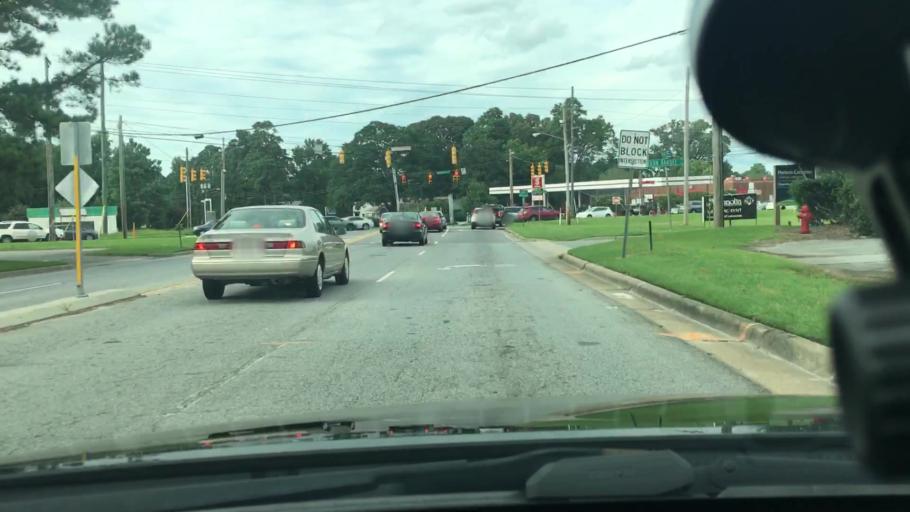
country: US
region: North Carolina
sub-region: Pitt County
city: Greenville
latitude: 35.5896
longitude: -77.3465
